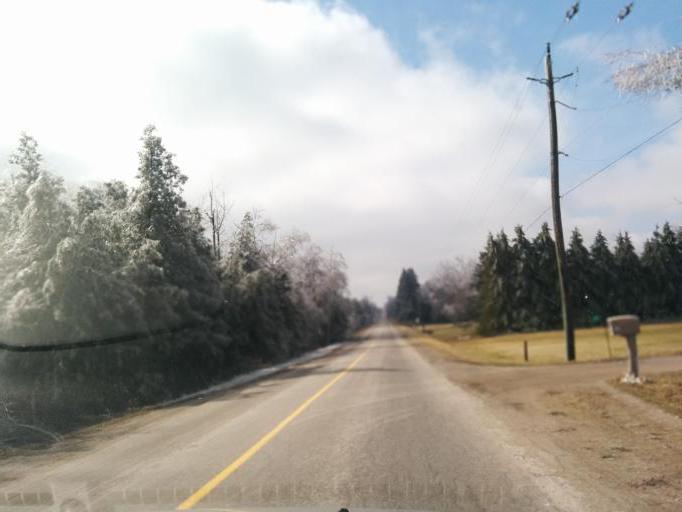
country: CA
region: Ontario
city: Waterloo
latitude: 43.6334
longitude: -80.5547
